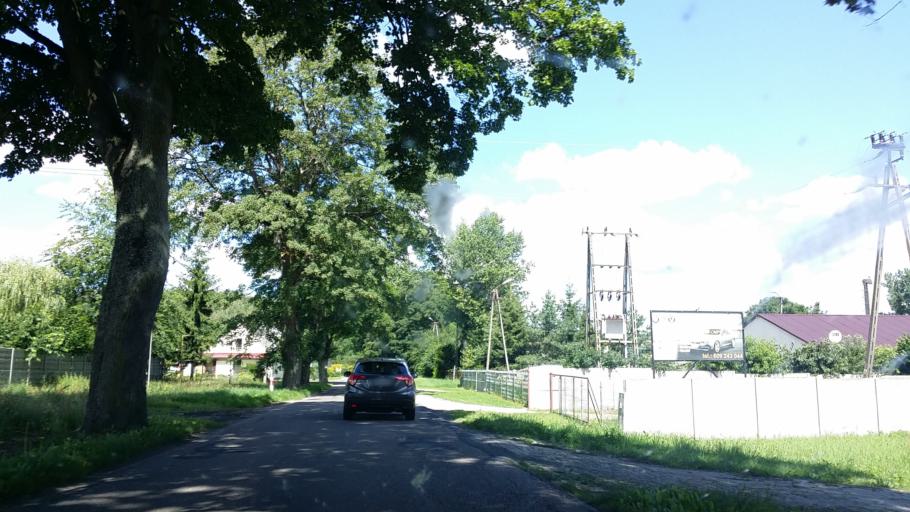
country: PL
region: West Pomeranian Voivodeship
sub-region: Powiat swidwinski
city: Swidwin
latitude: 53.7502
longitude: 15.7685
